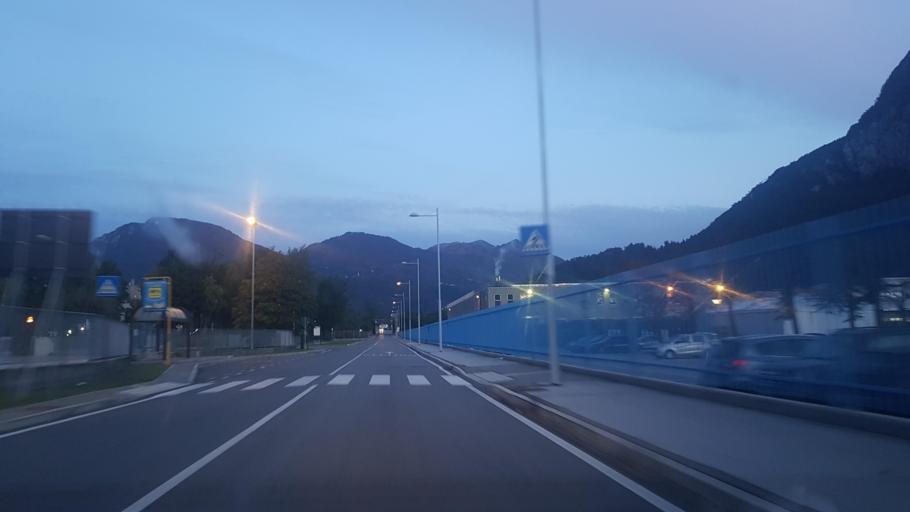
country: IT
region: Friuli Venezia Giulia
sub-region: Provincia di Udine
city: Tolmezzo
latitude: 46.3902
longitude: 13.0262
